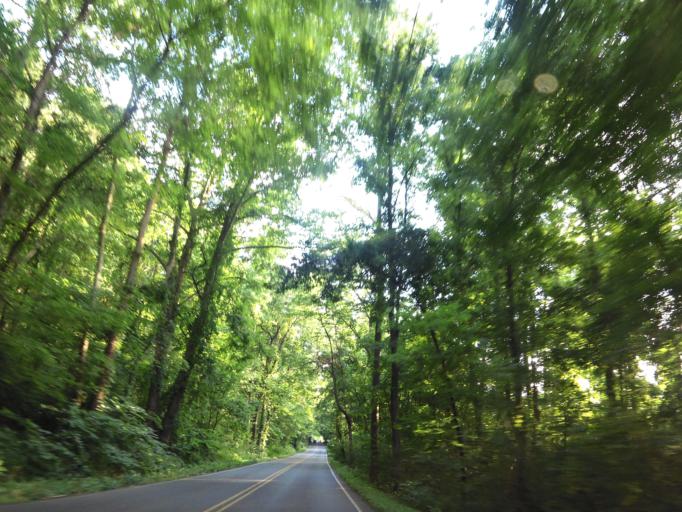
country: US
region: Tennessee
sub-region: Knox County
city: Knoxville
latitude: 36.0420
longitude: -83.9546
